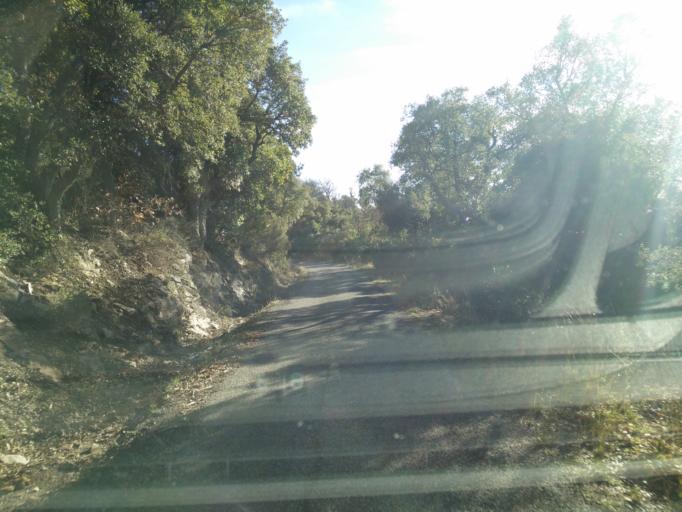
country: FR
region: Provence-Alpes-Cote d'Azur
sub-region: Departement du Var
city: Collobrieres
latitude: 43.2741
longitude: 6.3010
